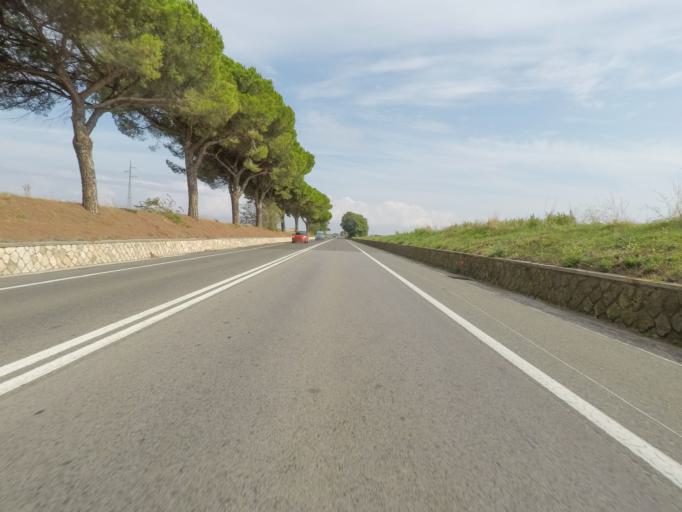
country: IT
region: Tuscany
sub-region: Provincia di Grosseto
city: Capalbio
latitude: 42.4147
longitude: 11.4170
